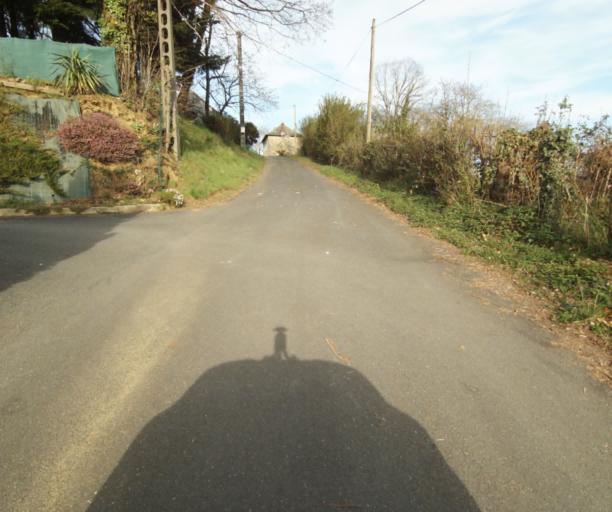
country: FR
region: Limousin
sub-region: Departement de la Correze
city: Naves
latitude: 45.3218
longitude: 1.7539
